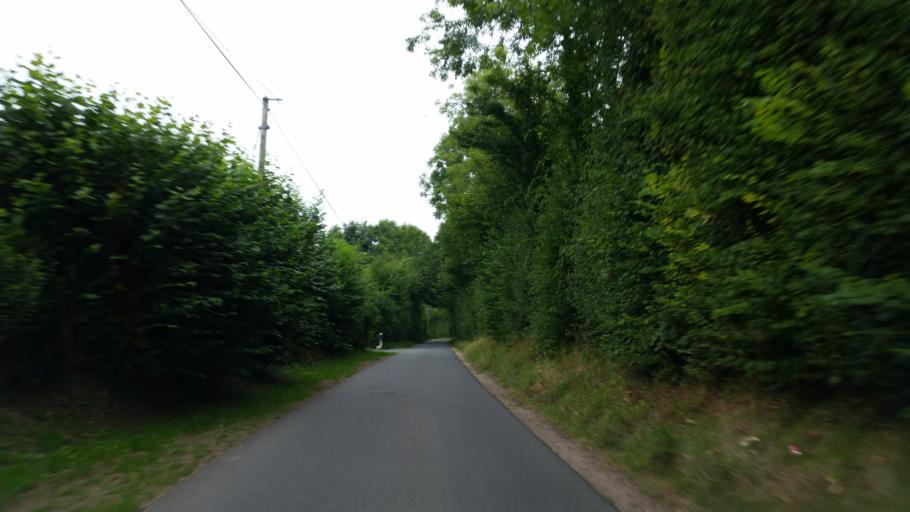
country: FR
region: Lower Normandy
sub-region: Departement du Calvados
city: Equemauville
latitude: 49.3983
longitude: 0.2276
